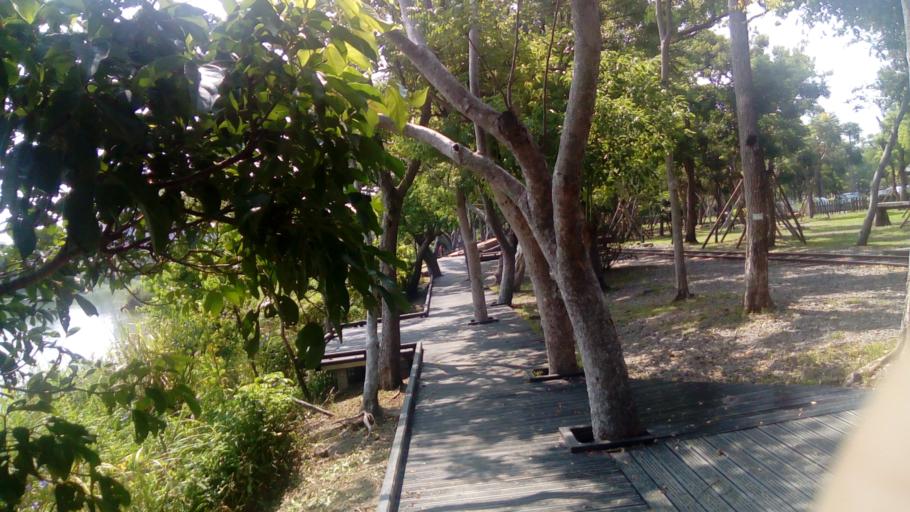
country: TW
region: Taiwan
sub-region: Yilan
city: Yilan
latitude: 24.6843
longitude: 121.7729
